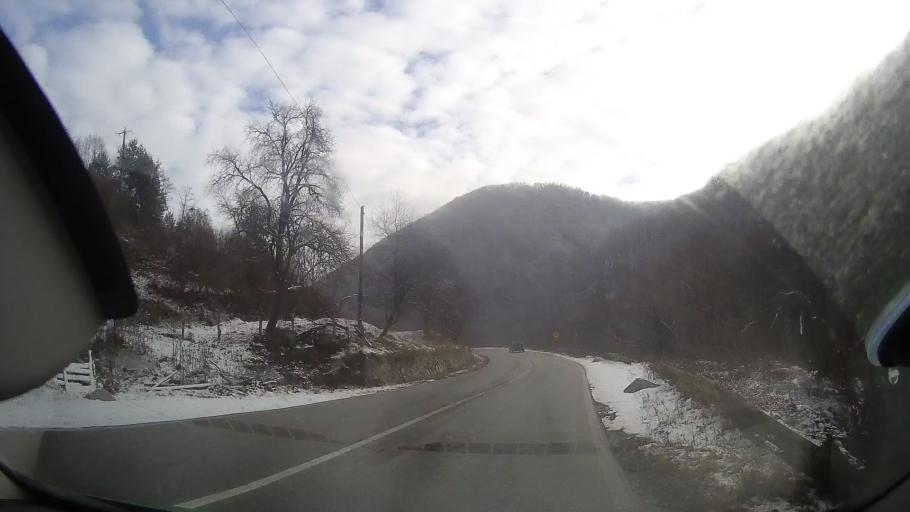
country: RO
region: Alba
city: Salciua de Sus
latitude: 46.3991
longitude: 23.3658
